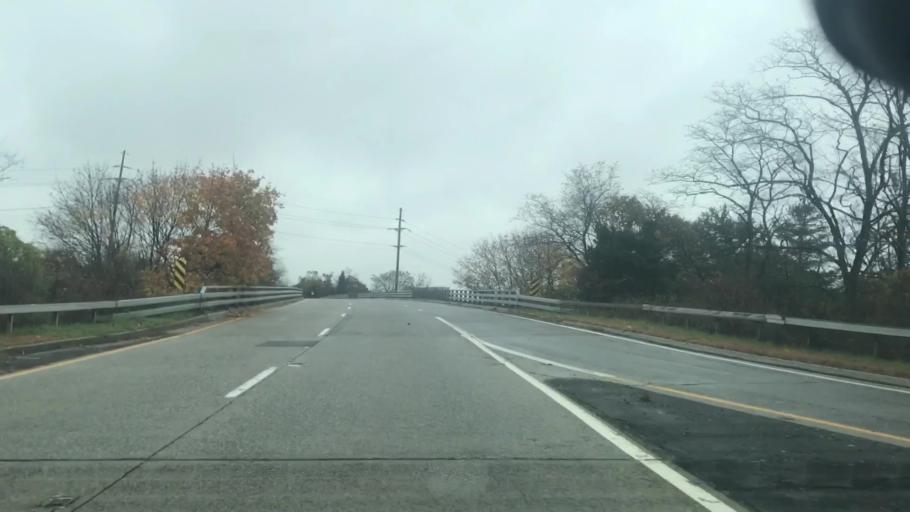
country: US
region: New York
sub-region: Suffolk County
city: West Islip
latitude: 40.7035
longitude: -73.3139
